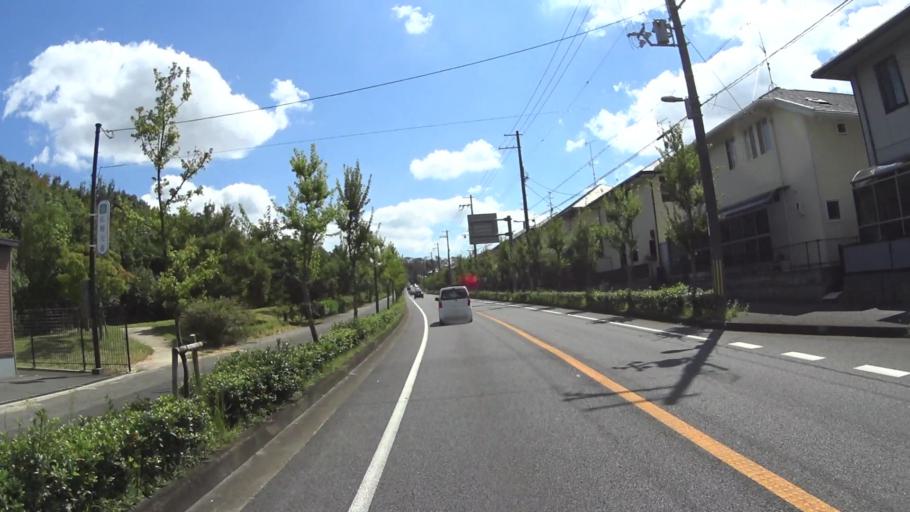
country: JP
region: Kyoto
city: Uji
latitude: 34.8687
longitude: 135.7946
